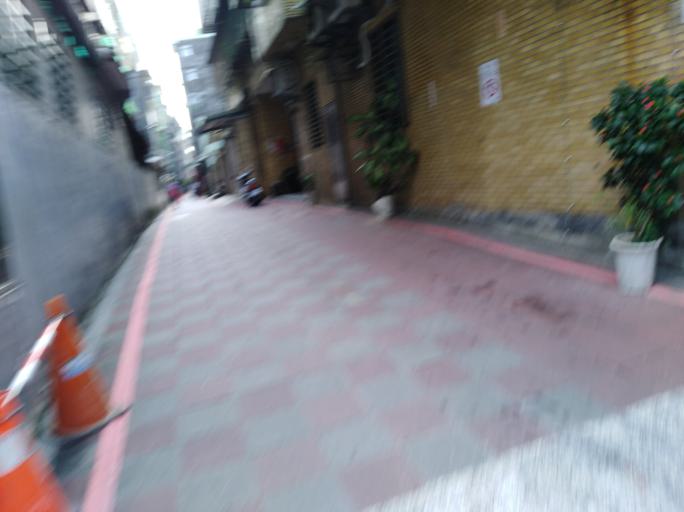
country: TW
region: Taipei
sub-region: Taipei
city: Banqiao
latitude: 25.0394
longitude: 121.4252
